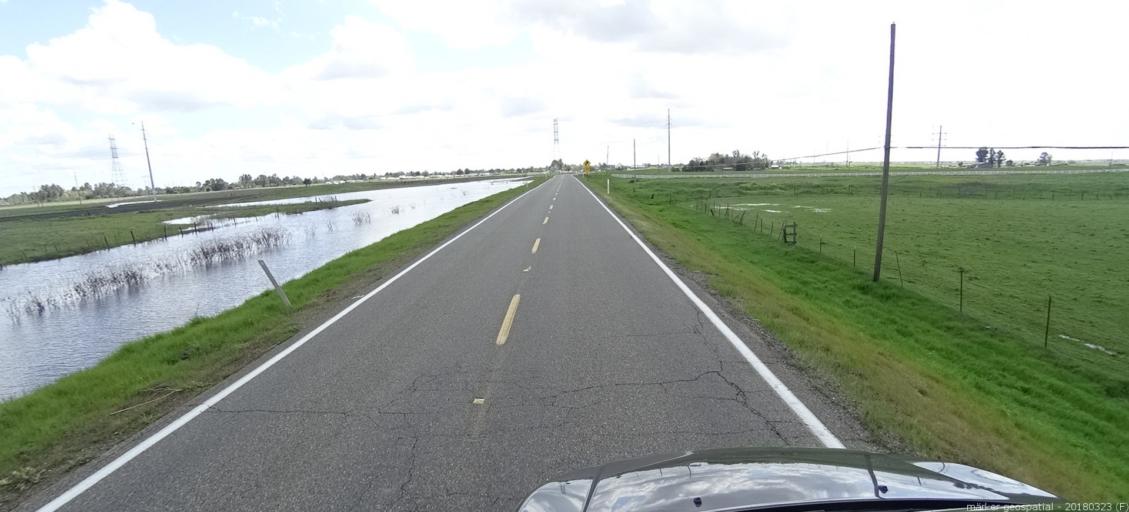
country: US
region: California
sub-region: Sacramento County
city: Elverta
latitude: 38.7082
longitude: -121.4864
